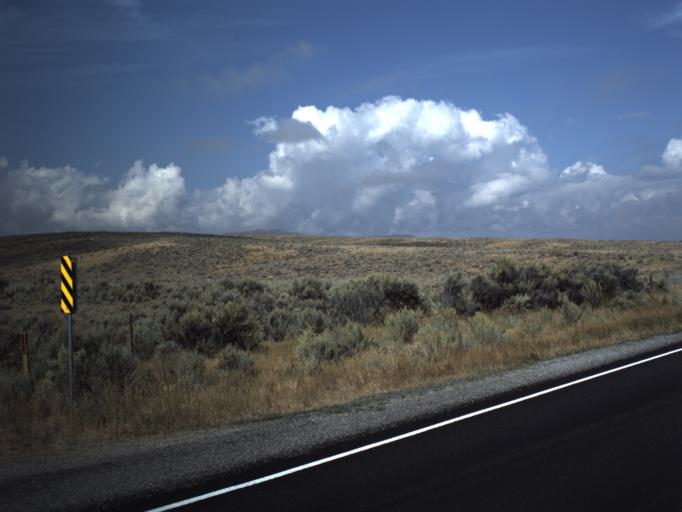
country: US
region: Utah
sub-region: Rich County
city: Randolph
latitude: 41.5698
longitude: -111.1609
